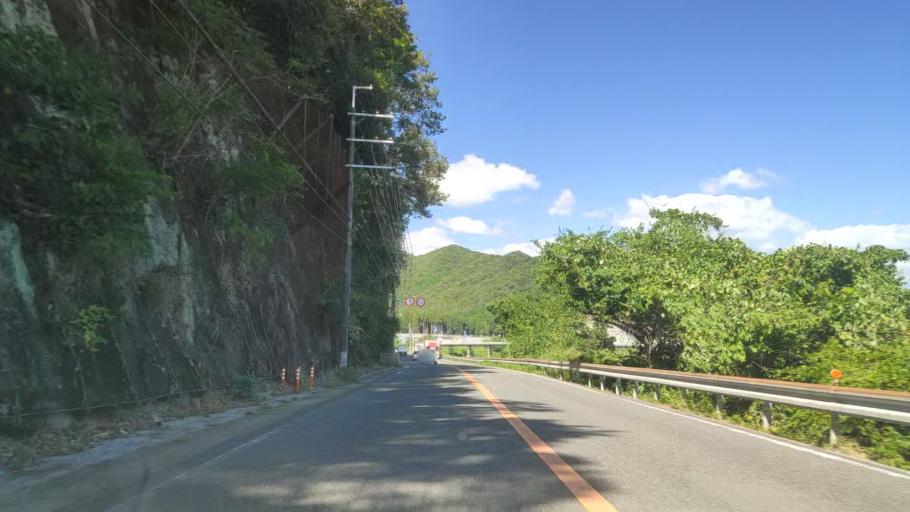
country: JP
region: Hyogo
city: Nishiwaki
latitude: 35.0175
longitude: 134.9873
